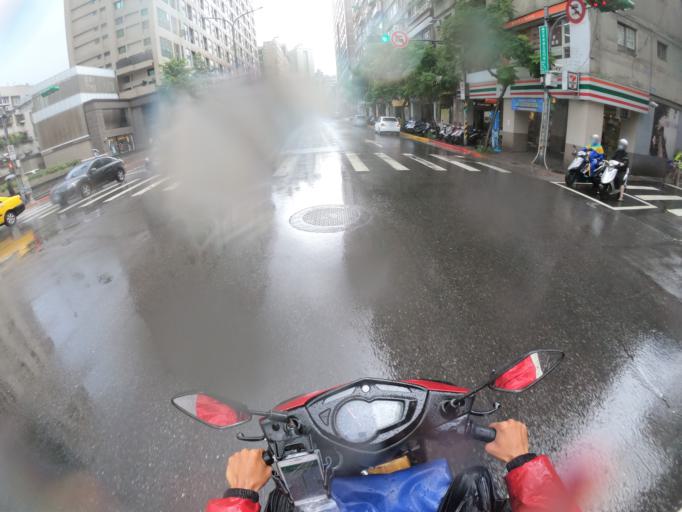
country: TW
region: Taipei
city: Taipei
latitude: 25.0407
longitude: 121.5738
